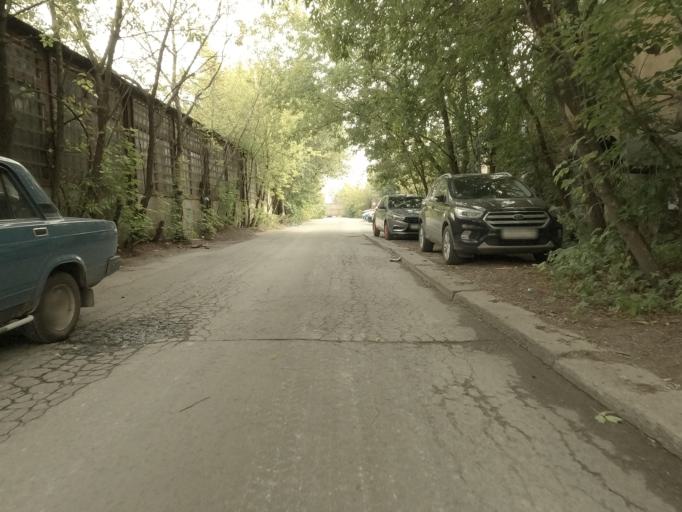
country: RU
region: St.-Petersburg
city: Admiralteisky
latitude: 59.8973
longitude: 30.2922
